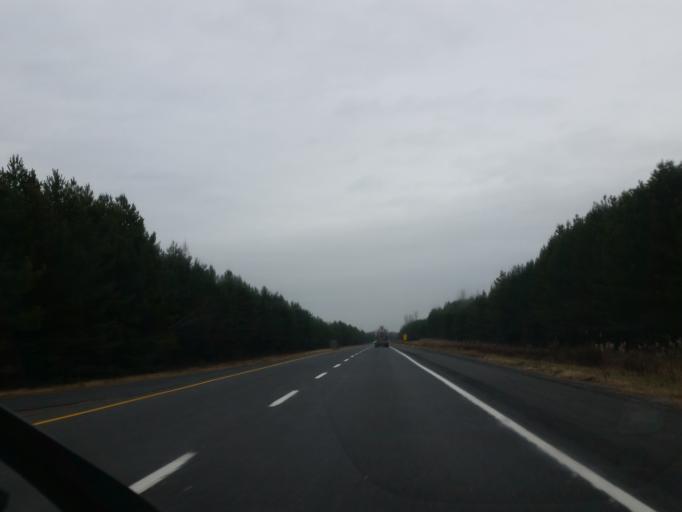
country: CA
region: Quebec
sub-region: Mauricie
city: Becancour
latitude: 46.5314
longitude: -72.2800
